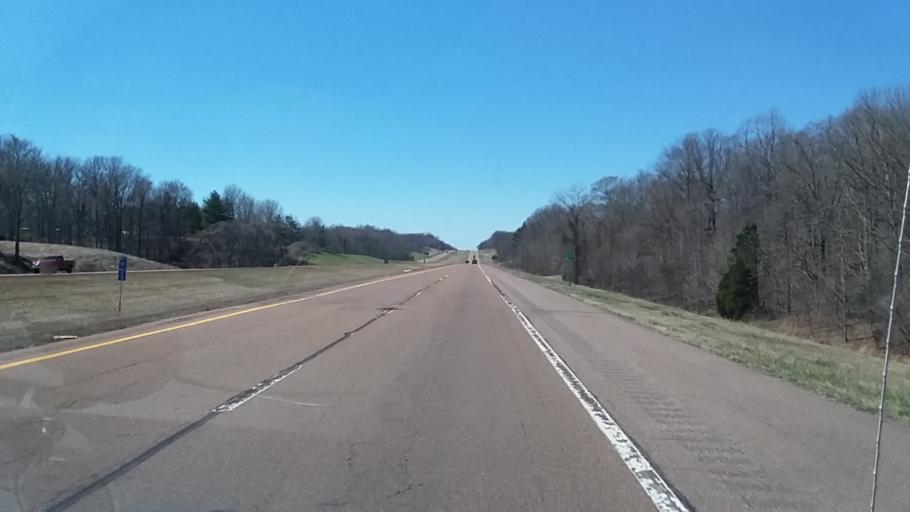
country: US
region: Tennessee
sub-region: Dyer County
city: Dyersburg
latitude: 36.0722
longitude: -89.4663
